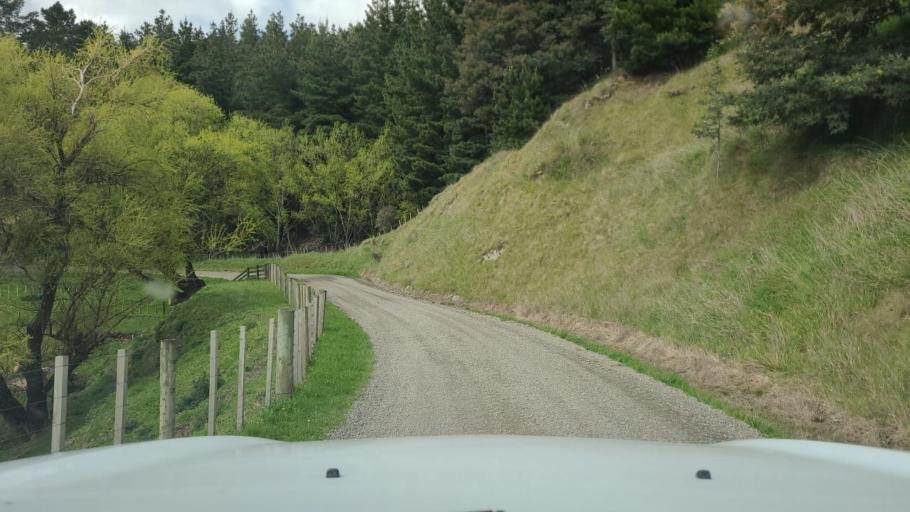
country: NZ
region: Wellington
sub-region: South Wairarapa District
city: Waipawa
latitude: -41.2159
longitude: 175.5962
